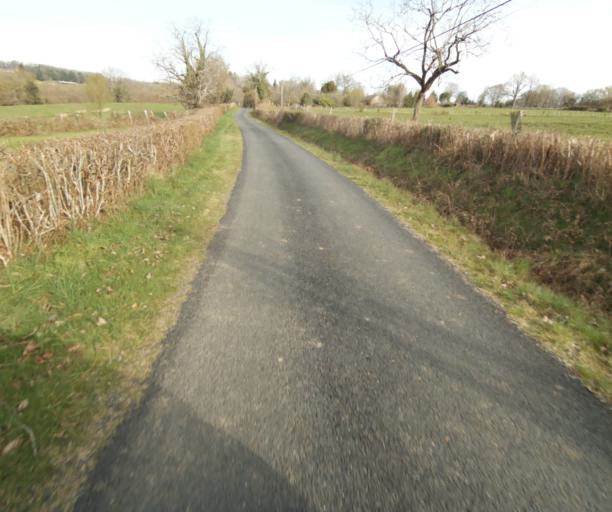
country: FR
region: Limousin
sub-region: Departement de la Correze
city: Chamboulive
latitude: 45.4184
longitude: 1.7655
